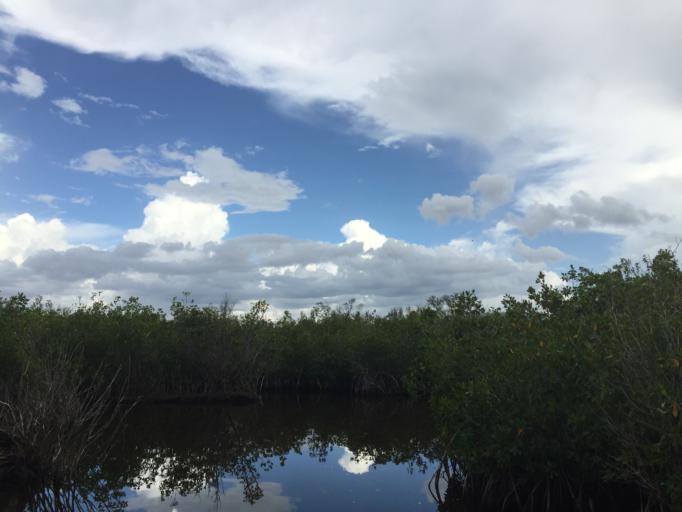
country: US
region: Florida
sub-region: Collier County
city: Marco
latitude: 25.9013
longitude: -81.3739
